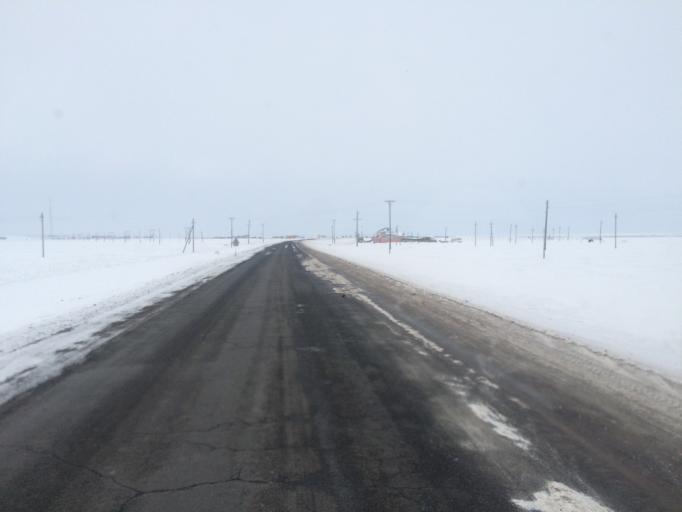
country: RU
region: Orenburg
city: Dombarovskiy
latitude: 49.9574
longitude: 60.0836
